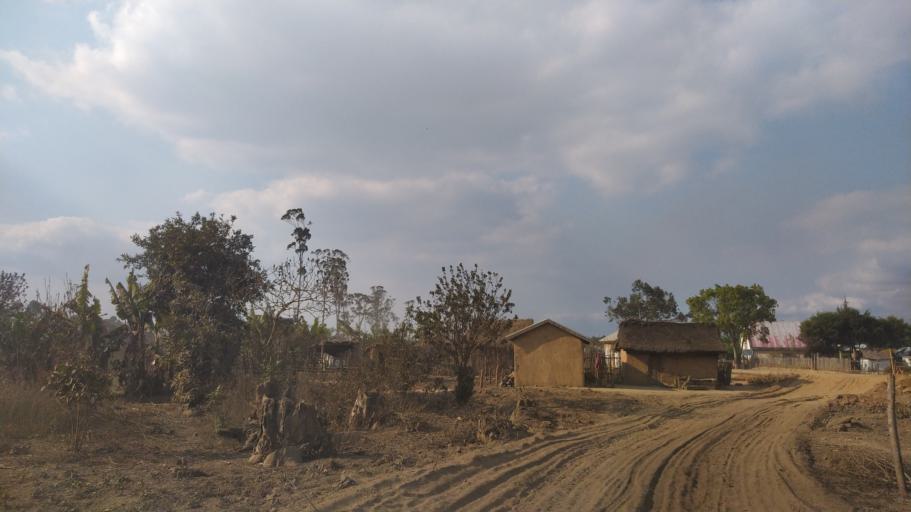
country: MG
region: Alaotra Mangoro
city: Moramanga
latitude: -18.6364
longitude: 48.2756
